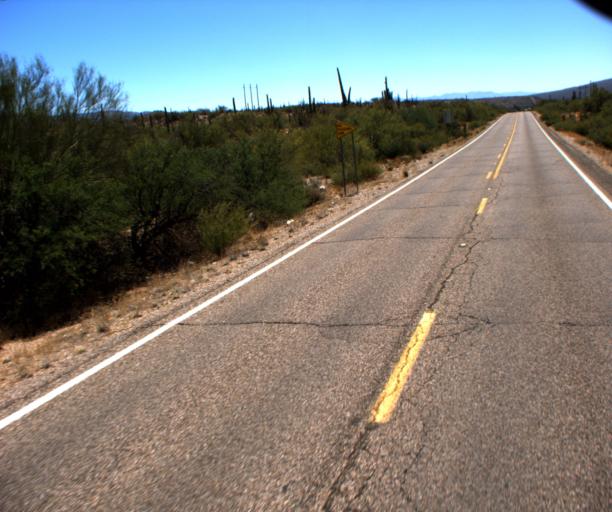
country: US
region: Arizona
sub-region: Pinal County
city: Kearny
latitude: 33.0570
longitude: -110.9020
